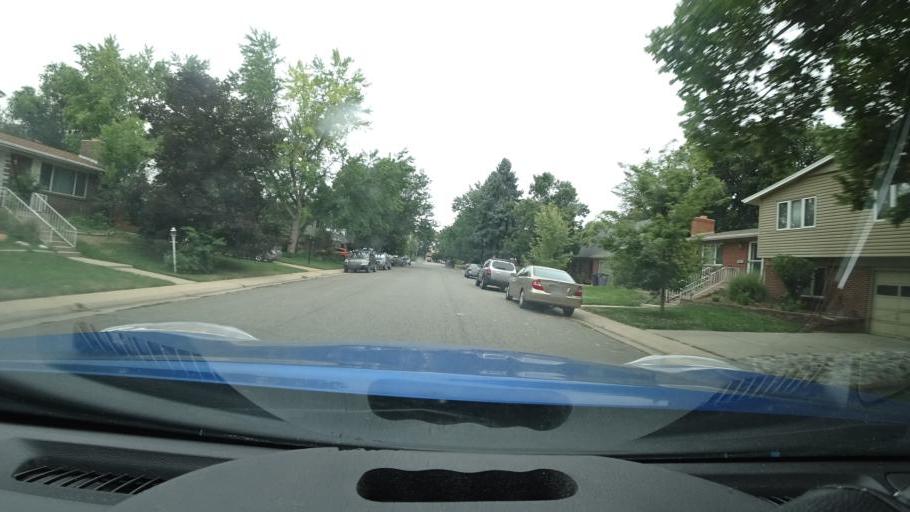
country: US
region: Colorado
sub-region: Arapahoe County
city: Glendale
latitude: 39.6814
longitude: -104.9151
